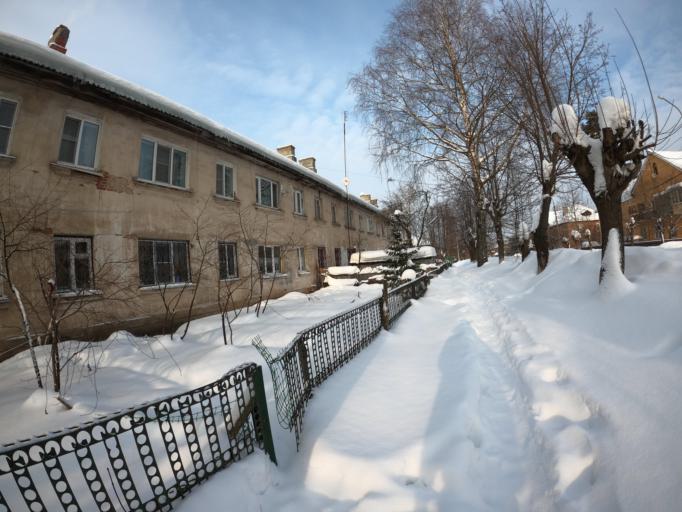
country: RU
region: Moskovskaya
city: Elektrogorsk
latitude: 55.8944
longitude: 38.7697
